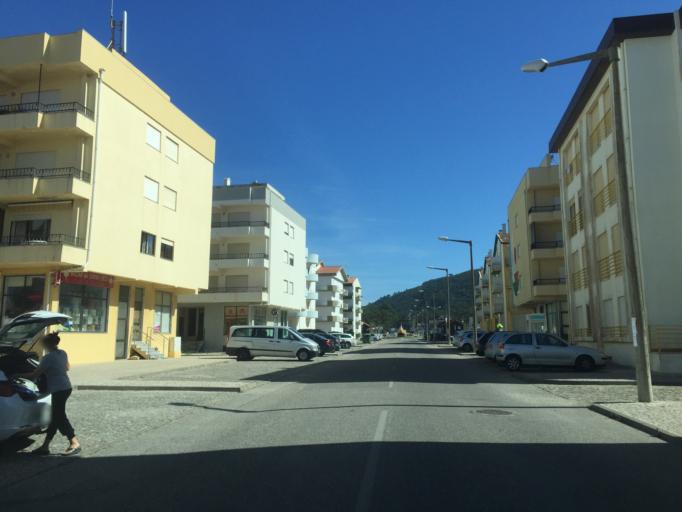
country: PT
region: Coimbra
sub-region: Figueira da Foz
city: Buarcos
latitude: 40.2166
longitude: -8.8925
